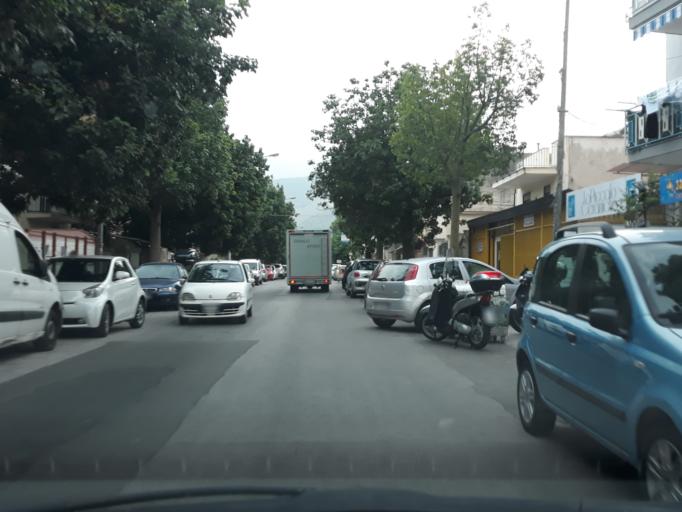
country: IT
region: Sicily
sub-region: Palermo
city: Monreale
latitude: 38.0953
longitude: 13.3191
